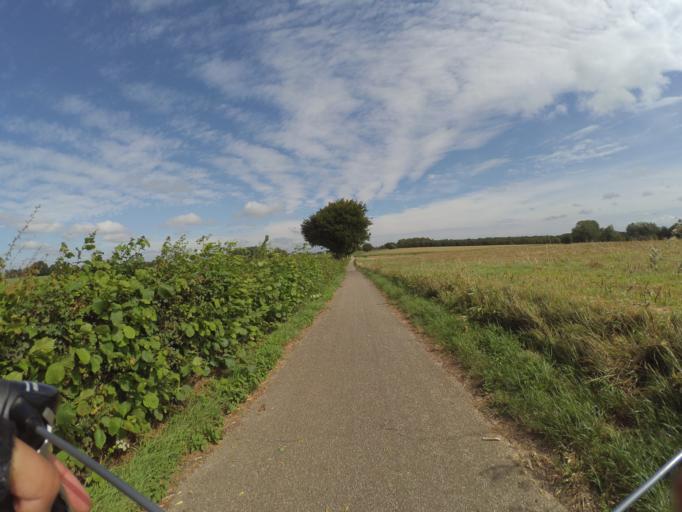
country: NL
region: Limburg
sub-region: Eijsden-Margraten
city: Margraten
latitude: 50.7917
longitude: 5.8360
